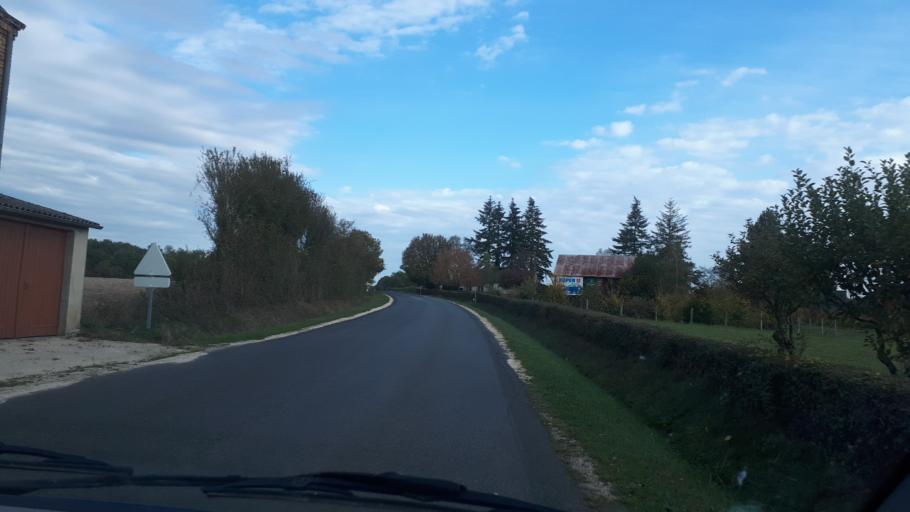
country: FR
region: Centre
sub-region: Departement du Loir-et-Cher
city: Mondoubleau
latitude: 47.9331
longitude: 0.9337
